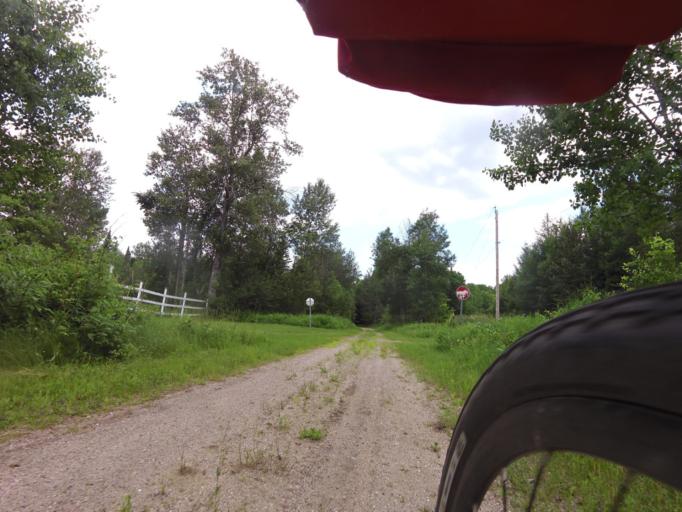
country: CA
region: Quebec
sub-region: Outaouais
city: Maniwaki
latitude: 46.0322
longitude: -76.0965
